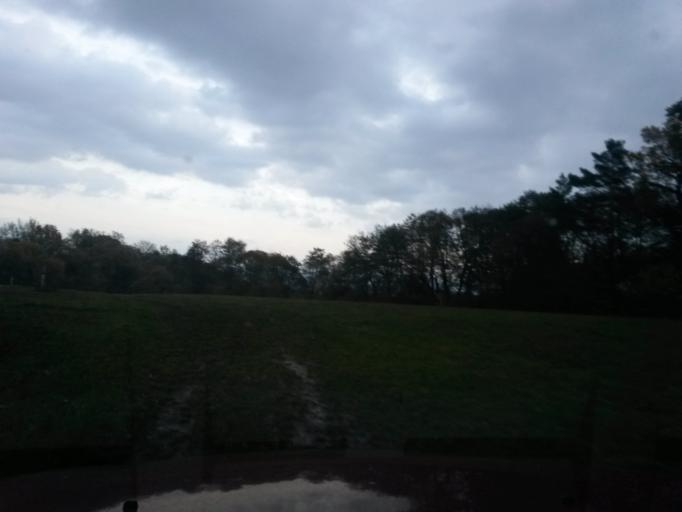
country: SK
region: Kosicky
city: Kosice
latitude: 48.7951
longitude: 21.2877
